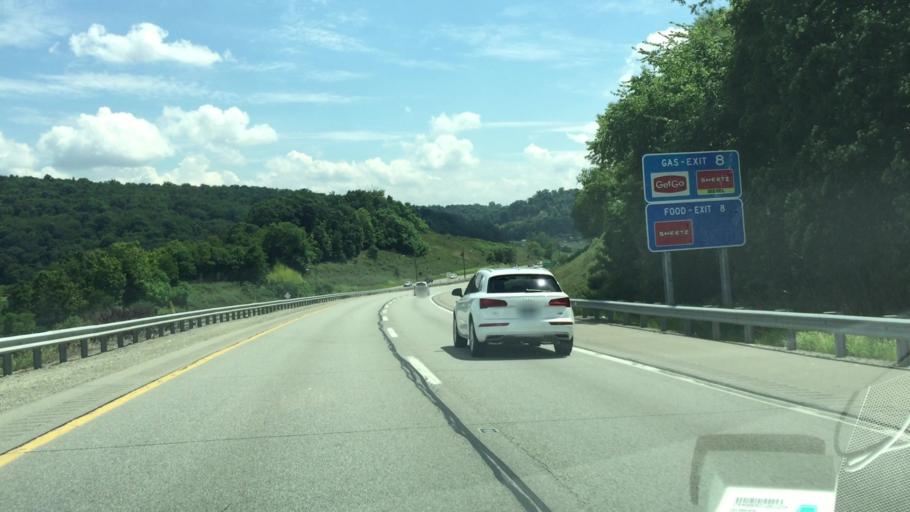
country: US
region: Pennsylvania
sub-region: Allegheny County
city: Ben Avon
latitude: 40.5341
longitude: -80.0742
